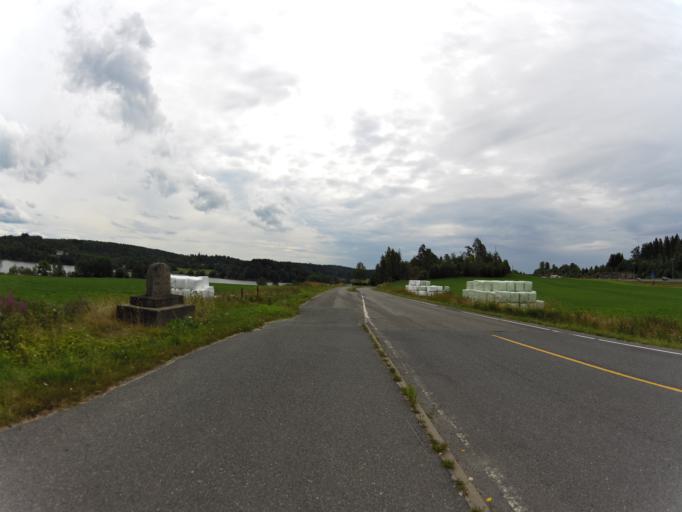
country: NO
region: Akershus
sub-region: As
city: As
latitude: 59.6860
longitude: 10.7391
